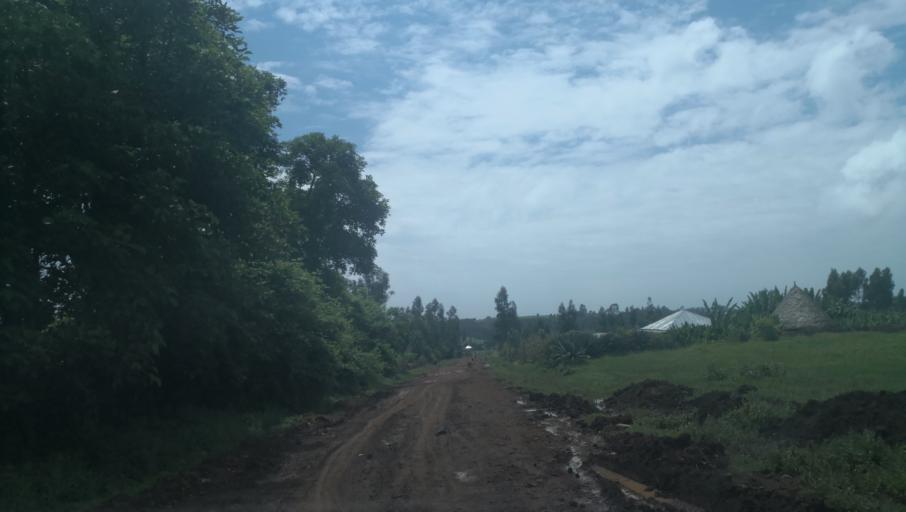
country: ET
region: Southern Nations, Nationalities, and People's Region
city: Butajira
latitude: 8.3039
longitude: 38.4659
